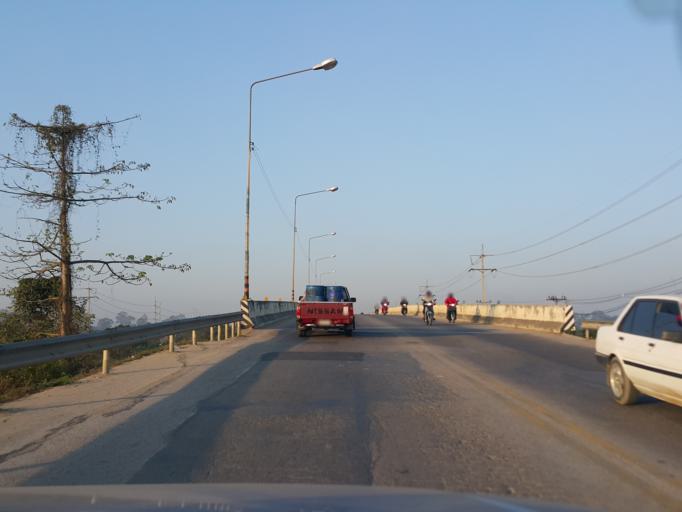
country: TH
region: Chiang Mai
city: Saraphi
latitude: 18.7339
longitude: 99.0334
